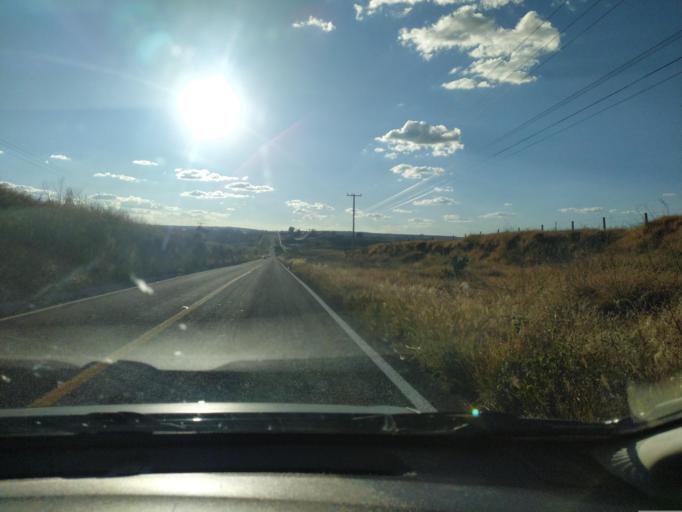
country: MX
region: Jalisco
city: San Diego de Alejandria
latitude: 21.0240
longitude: -101.9392
